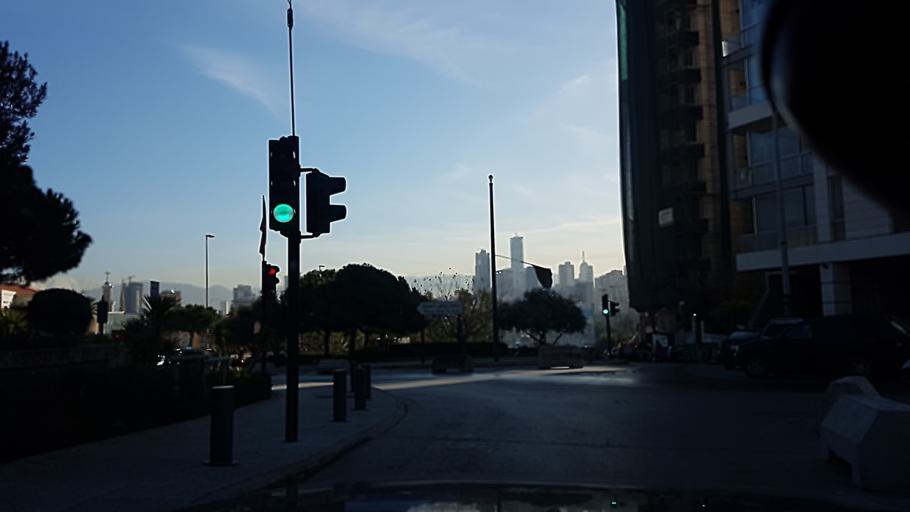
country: LB
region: Beyrouth
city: Beirut
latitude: 33.8942
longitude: 35.4991
